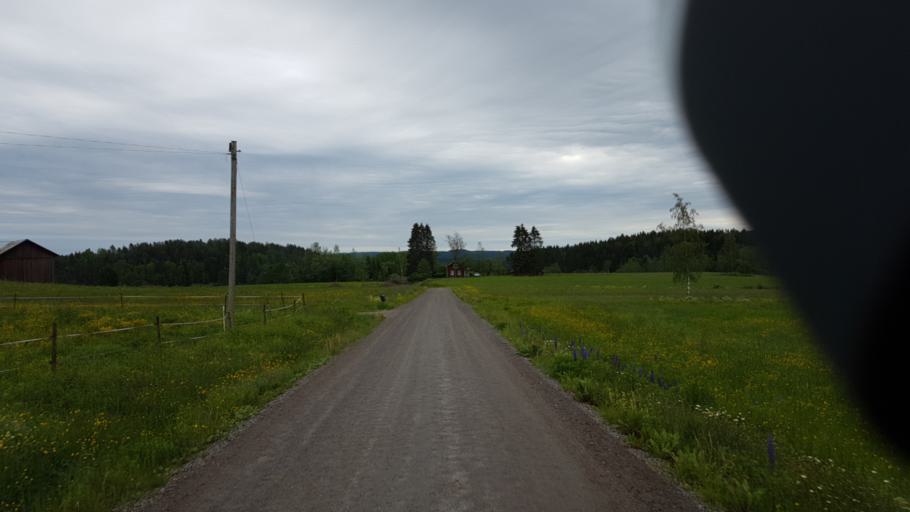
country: NO
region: Ostfold
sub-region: Romskog
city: Romskog
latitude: 59.7004
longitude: 12.0632
